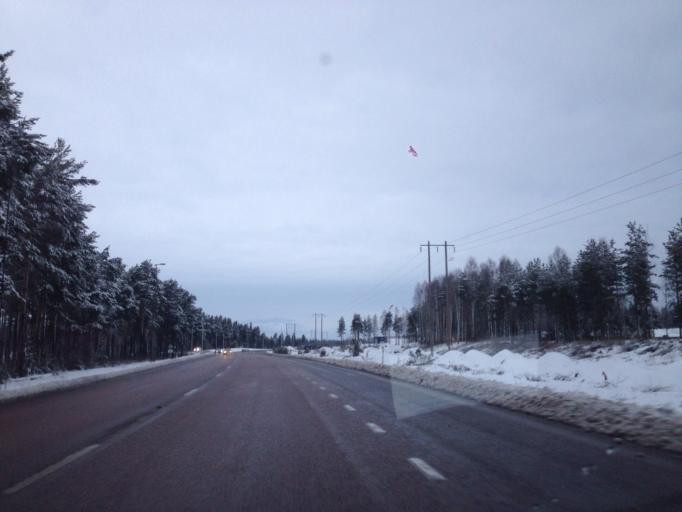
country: SE
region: Dalarna
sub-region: Mora Kommun
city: Mora
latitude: 61.0141
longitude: 14.5905
